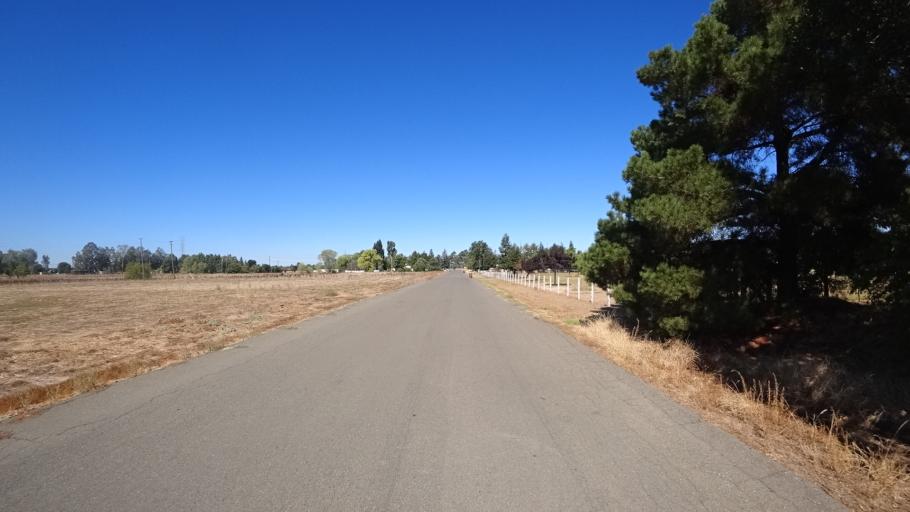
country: US
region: California
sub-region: Sacramento County
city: Wilton
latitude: 38.4208
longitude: -121.3067
